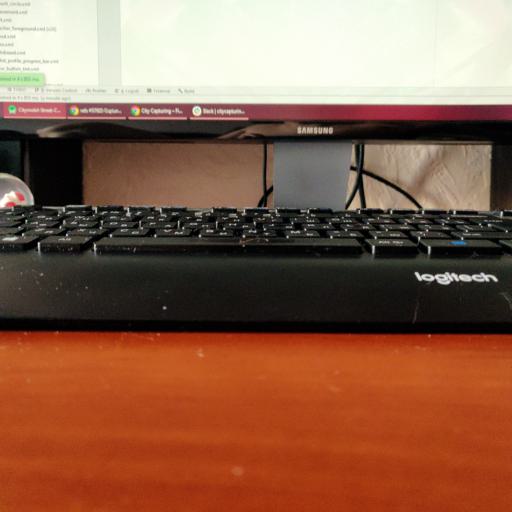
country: EE
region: Hiiumaa
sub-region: Kaerdla linn
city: Kardla
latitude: 58.6310
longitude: 22.6176
